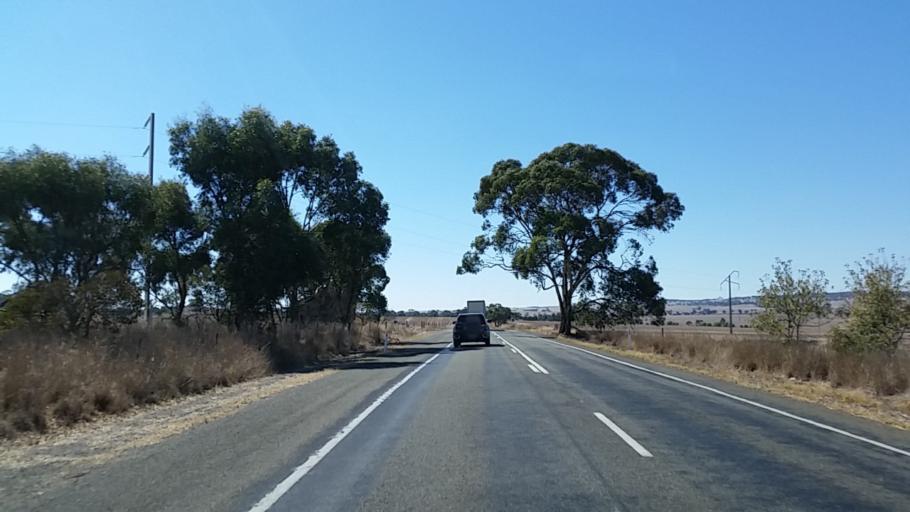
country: AU
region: South Australia
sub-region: Clare and Gilbert Valleys
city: Clare
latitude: -34.0227
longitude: 138.8062
